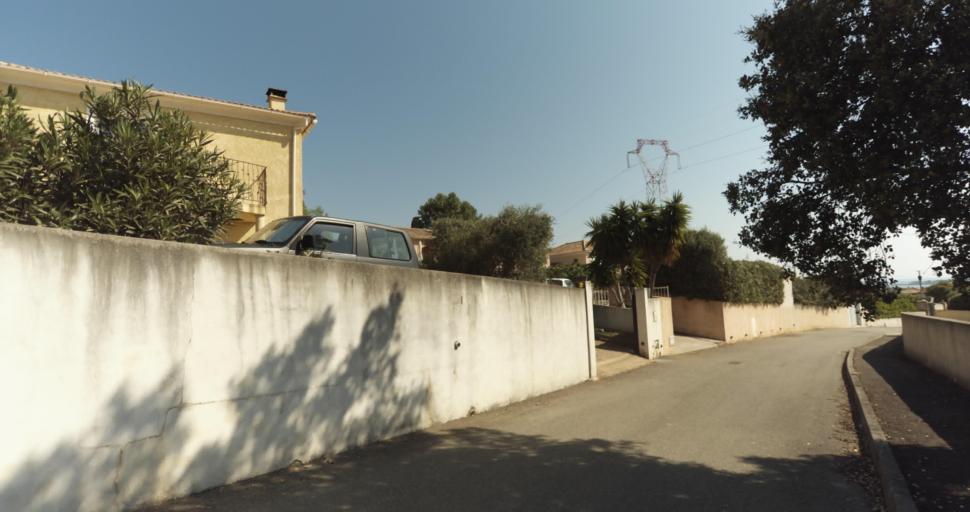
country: FR
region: Corsica
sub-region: Departement de la Haute-Corse
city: Biguglia
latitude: 42.6250
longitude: 9.4238
